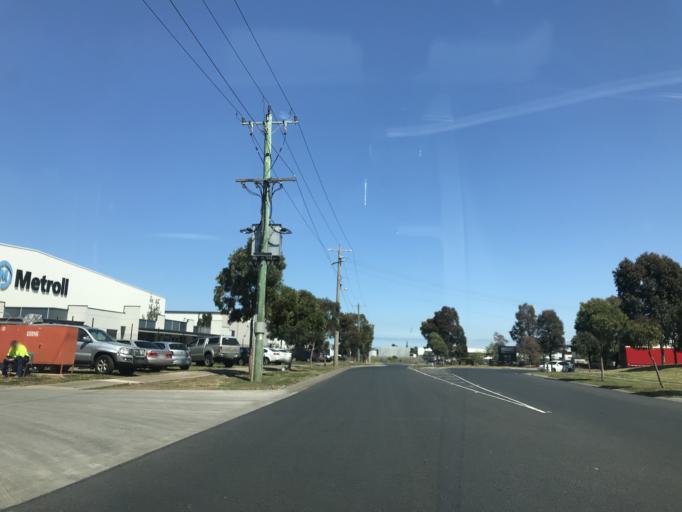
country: AU
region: Victoria
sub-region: Brimbank
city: Derrimut
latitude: -37.8161
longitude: 144.7820
